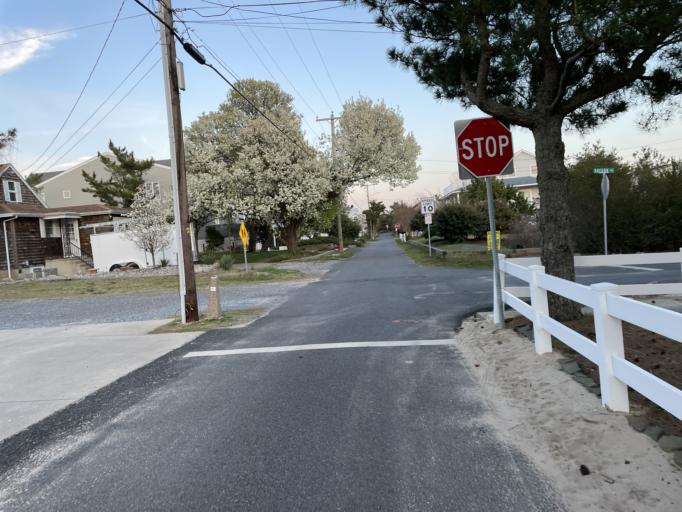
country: US
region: Delaware
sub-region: Sussex County
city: Lewes
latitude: 38.7840
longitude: -75.1454
